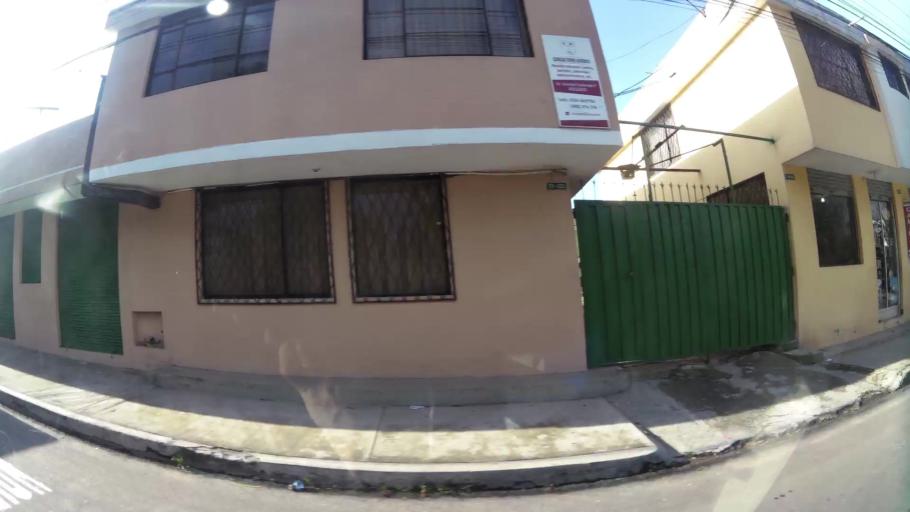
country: EC
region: Pichincha
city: Sangolqui
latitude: -0.2984
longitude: -78.4683
